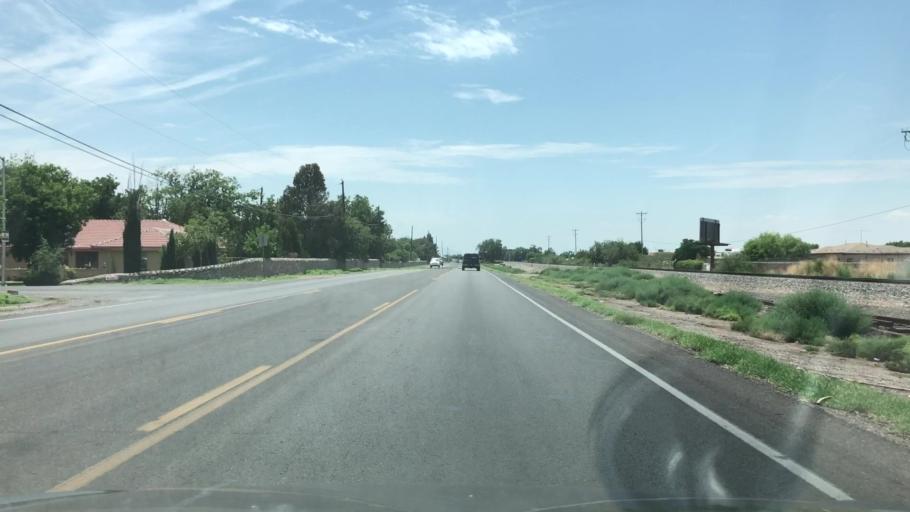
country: US
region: New Mexico
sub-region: Dona Ana County
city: University Park
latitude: 32.2662
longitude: -106.7609
